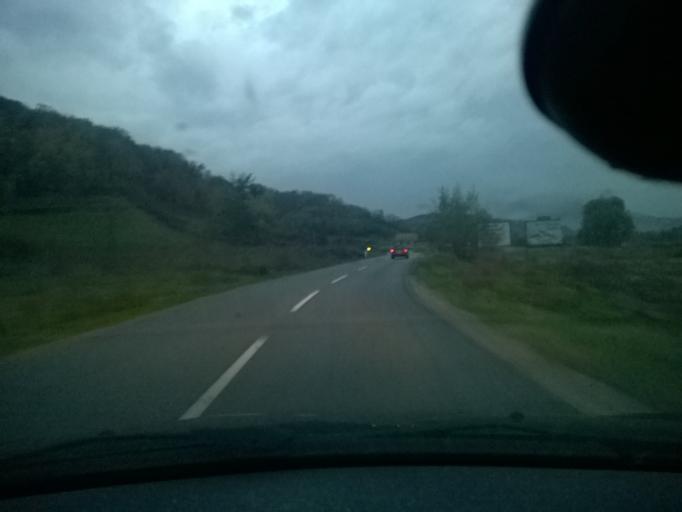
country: HR
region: Krapinsko-Zagorska
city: Zabok
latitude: 46.0482
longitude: 15.9089
